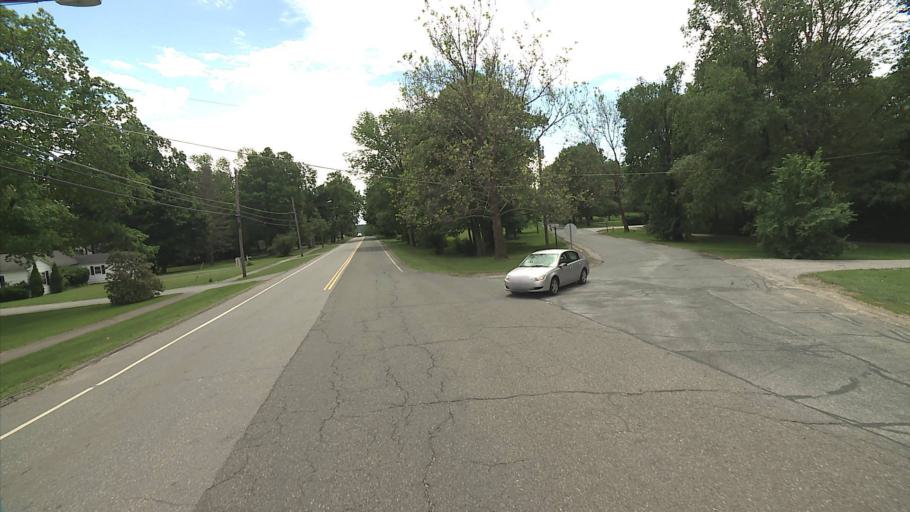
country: US
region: Connecticut
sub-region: Litchfield County
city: Litchfield
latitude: 41.7398
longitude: -73.1871
